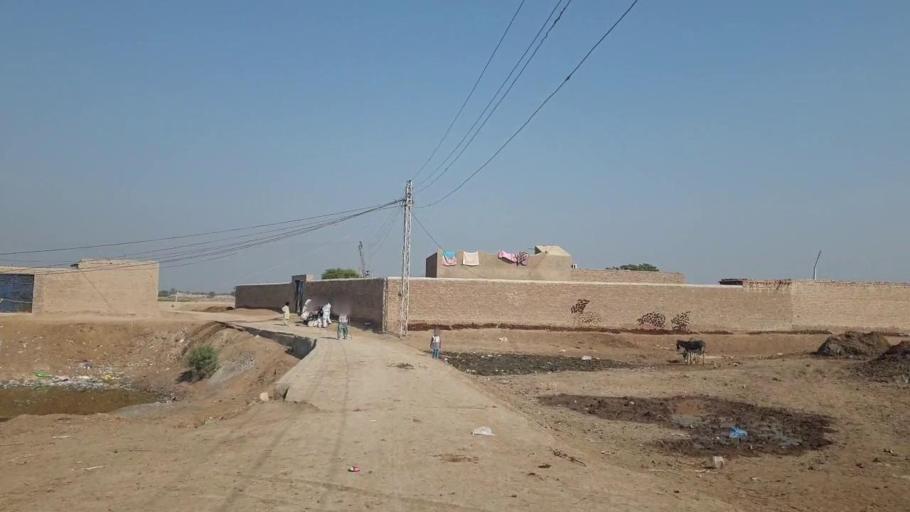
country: PK
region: Sindh
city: Bhan
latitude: 26.4407
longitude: 67.7319
